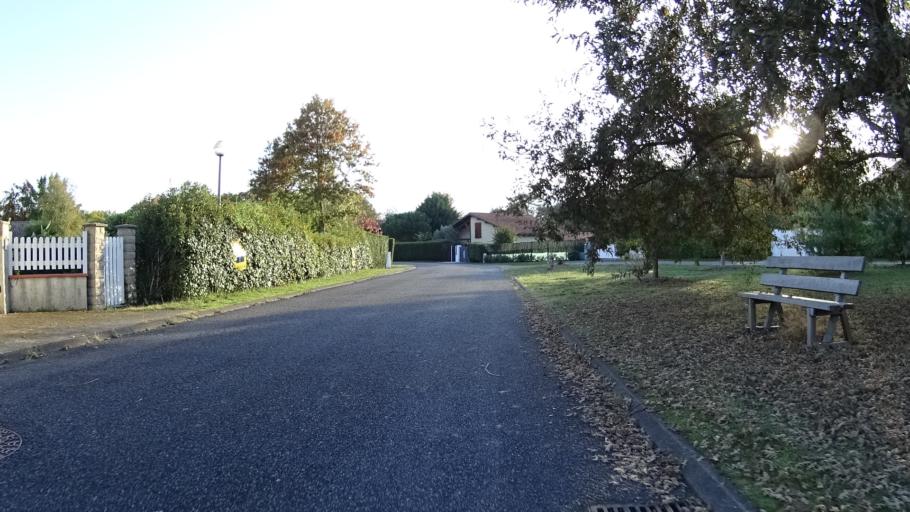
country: FR
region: Aquitaine
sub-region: Departement des Landes
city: Saint-Paul-les-Dax
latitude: 43.7390
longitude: -1.0477
